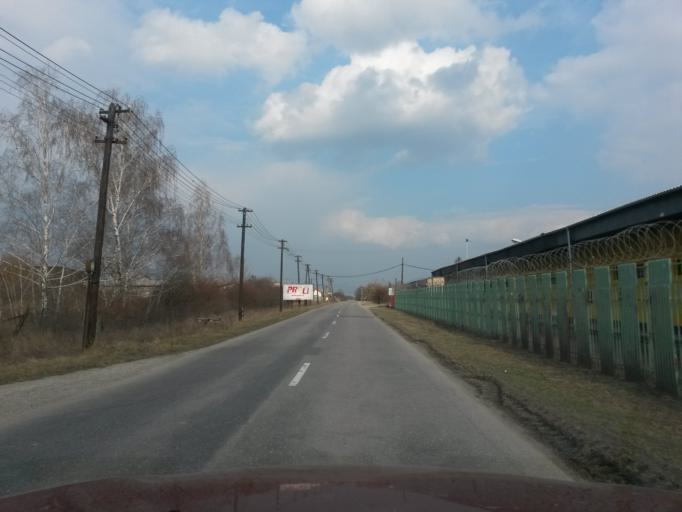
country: HU
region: Borsod-Abauj-Zemplen
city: Gonc
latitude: 48.5806
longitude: 21.2229
